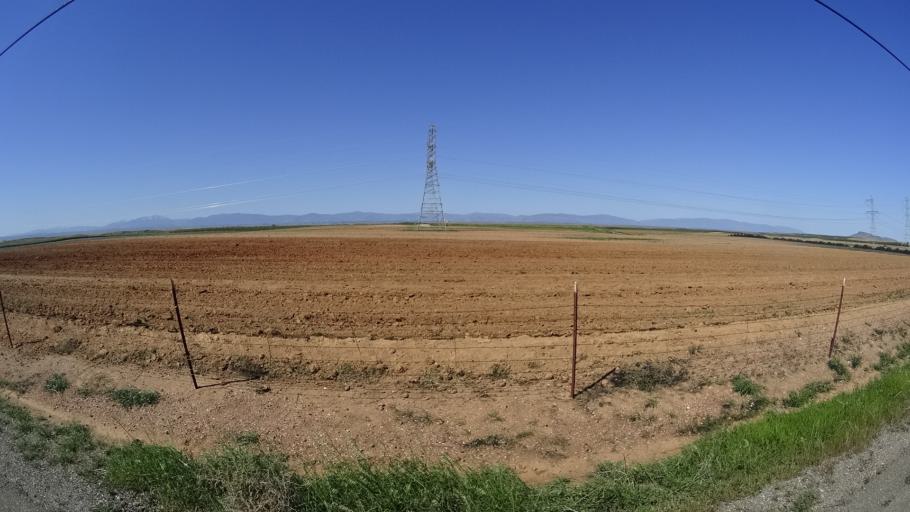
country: US
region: California
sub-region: Glenn County
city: Orland
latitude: 39.6739
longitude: -122.2718
